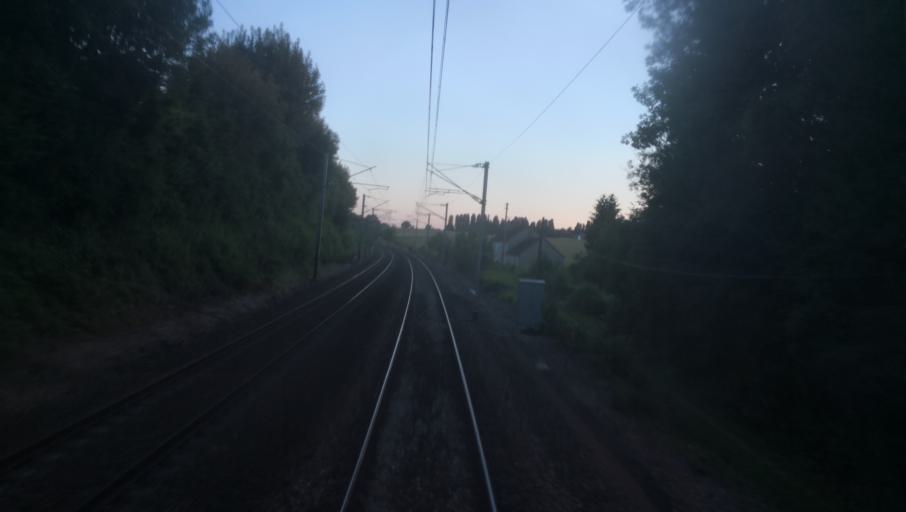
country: FR
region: Ile-de-France
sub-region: Departement des Yvelines
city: Longnes
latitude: 48.9635
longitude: 1.5924
